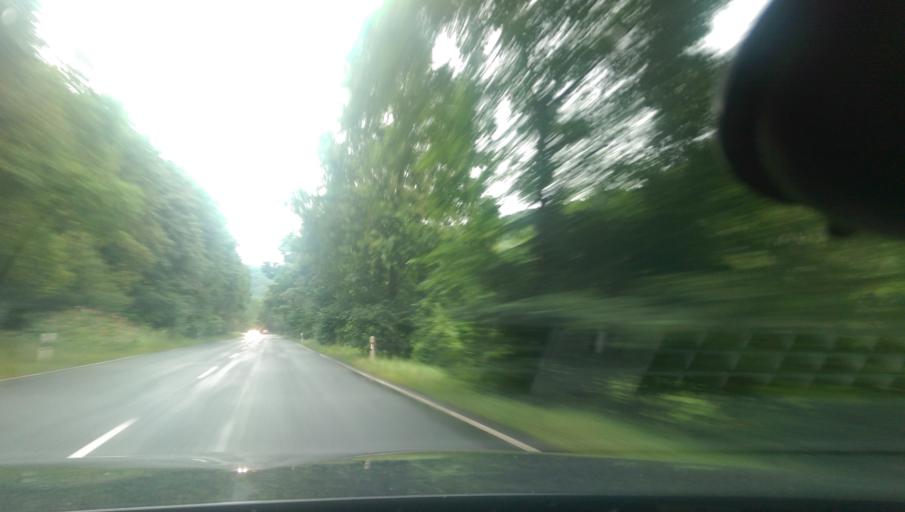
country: DE
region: Hesse
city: Witzenhausen
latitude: 51.3031
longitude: 9.8524
